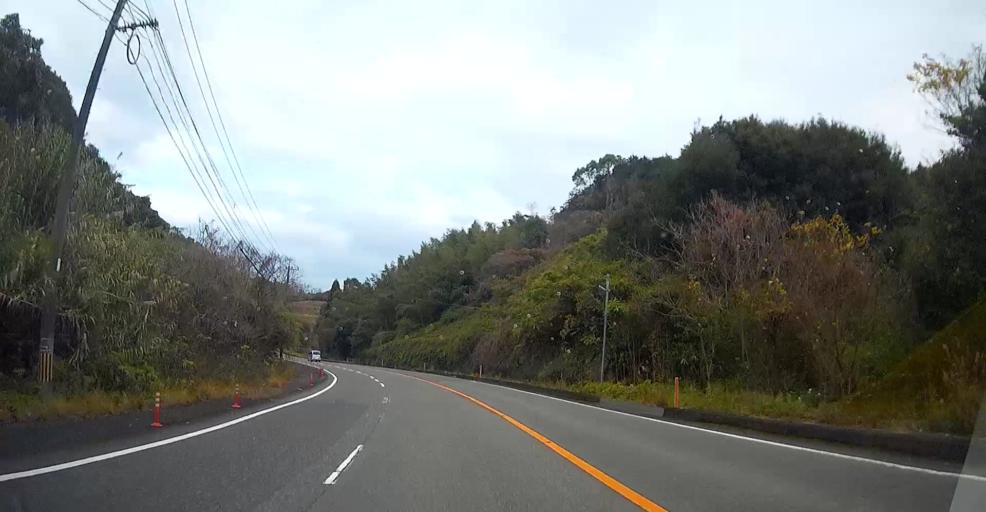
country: JP
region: Kumamoto
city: Hondo
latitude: 32.4952
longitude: 130.2988
